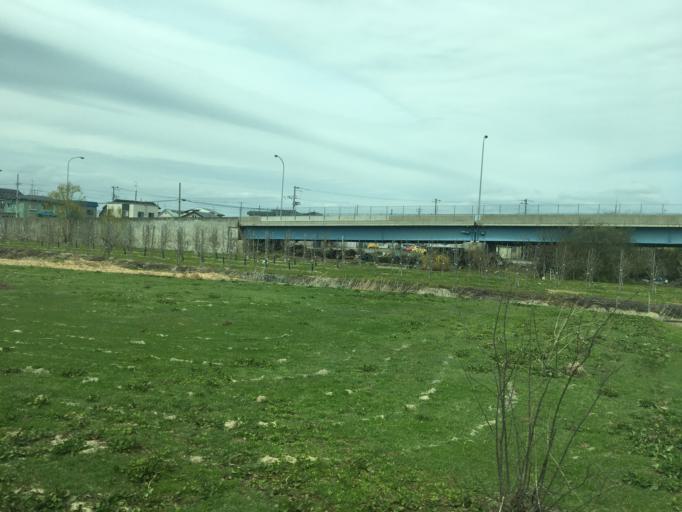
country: JP
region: Aomori
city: Kuroishi
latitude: 40.6439
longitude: 140.5176
